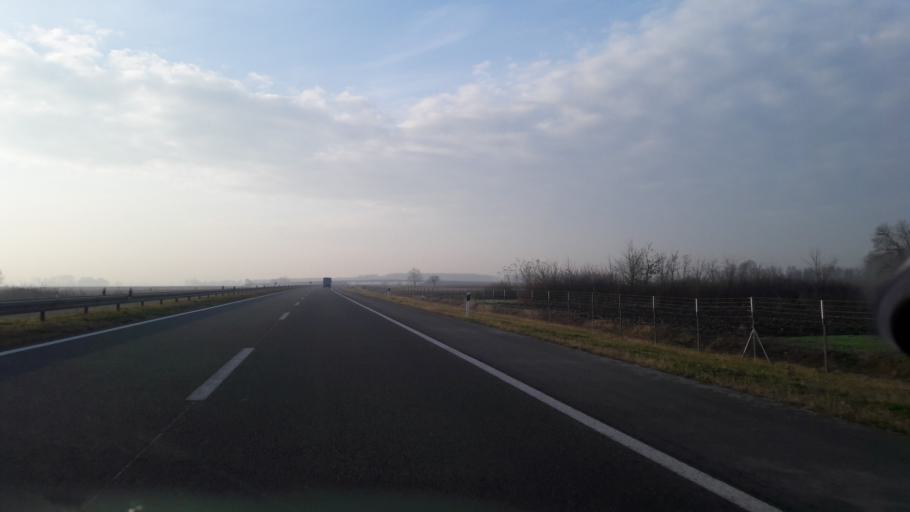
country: HR
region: Osjecko-Baranjska
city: Vuka
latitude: 45.4364
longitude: 18.4596
